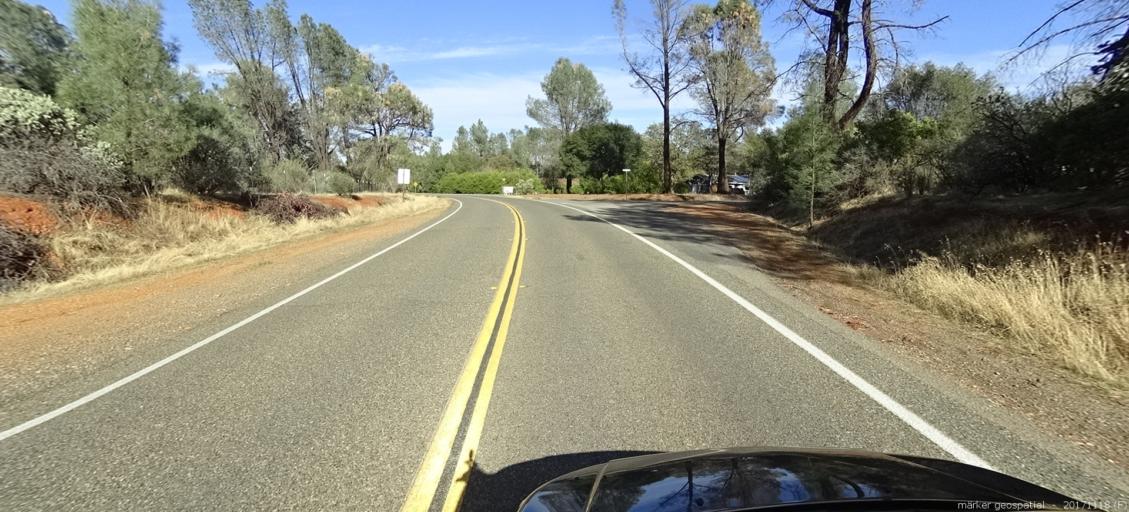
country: US
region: California
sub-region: Shasta County
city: Anderson
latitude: 40.4625
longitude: -122.3972
